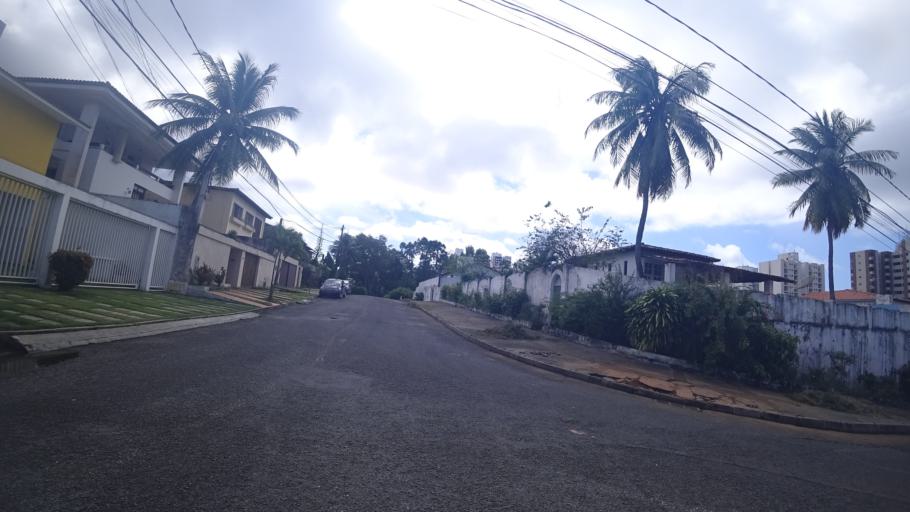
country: BR
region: Bahia
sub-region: Salvador
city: Salvador
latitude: -12.9921
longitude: -38.4634
